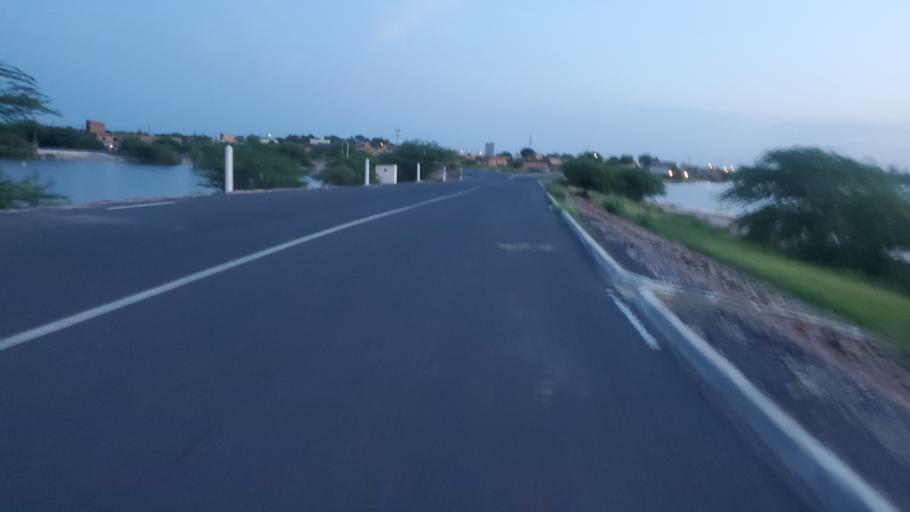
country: SN
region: Saint-Louis
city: Saint-Louis
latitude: 16.0733
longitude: -16.3891
